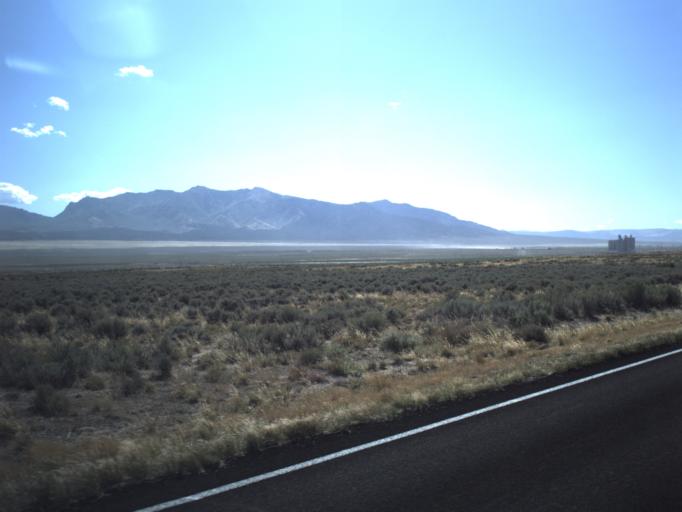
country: US
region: Utah
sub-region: Beaver County
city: Milford
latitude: 38.4147
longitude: -113.0099
